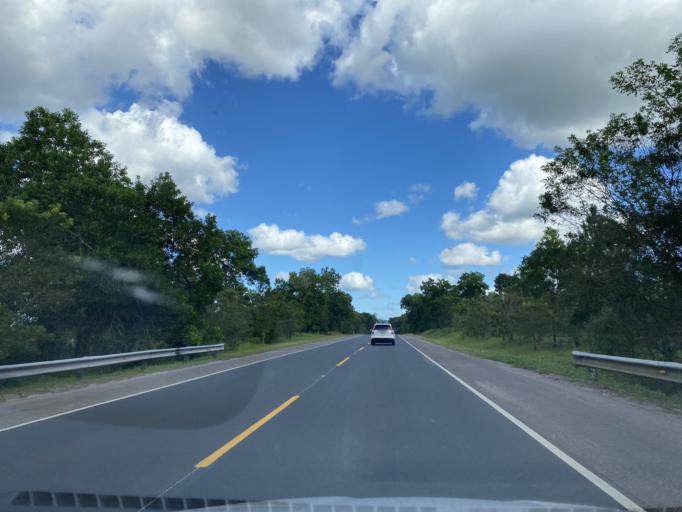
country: DO
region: Monte Plata
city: Monte Plata
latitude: 18.7783
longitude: -69.7439
